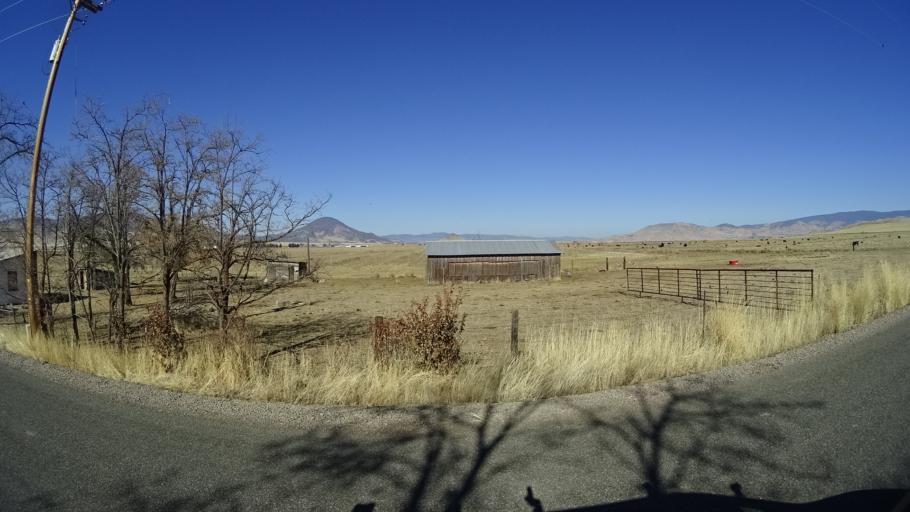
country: US
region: California
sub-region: Siskiyou County
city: Montague
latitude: 41.7559
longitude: -122.4739
